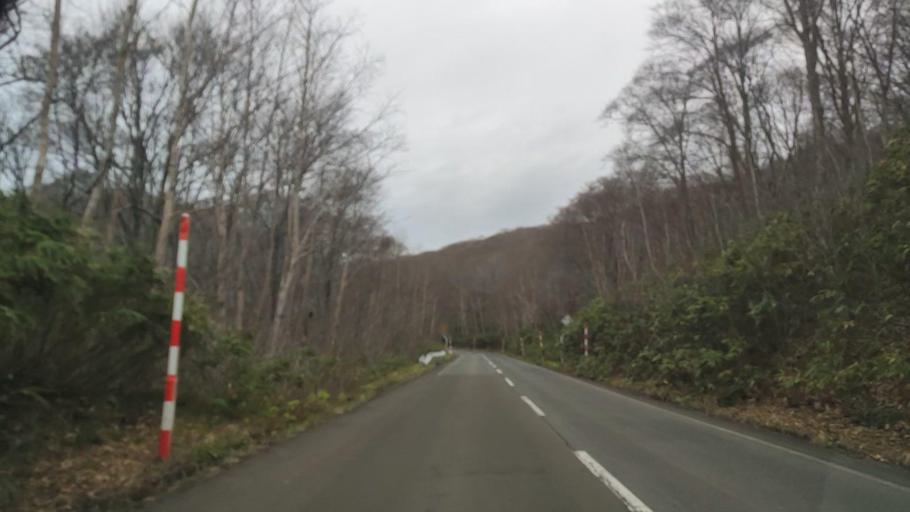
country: JP
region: Akita
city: Hanawa
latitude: 40.4204
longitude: 140.8366
